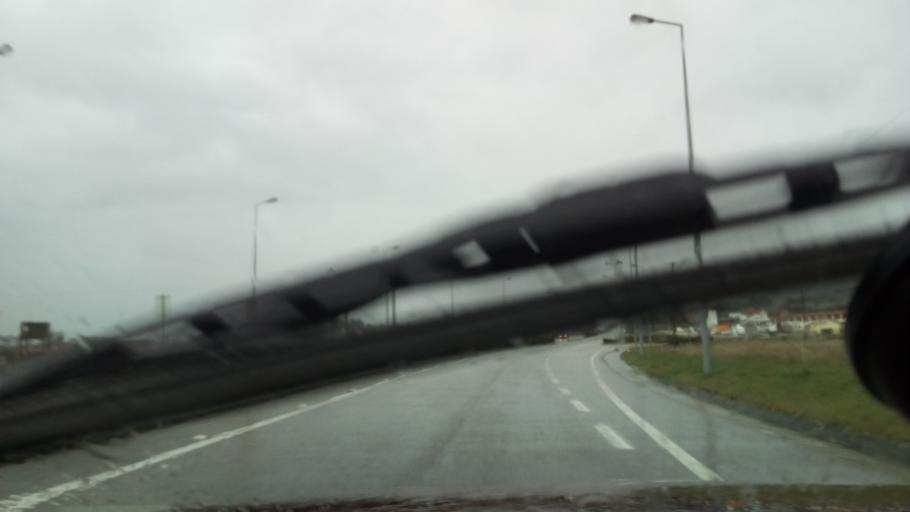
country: PT
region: Guarda
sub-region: Fornos de Algodres
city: Fornos de Algodres
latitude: 40.5362
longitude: -7.5648
